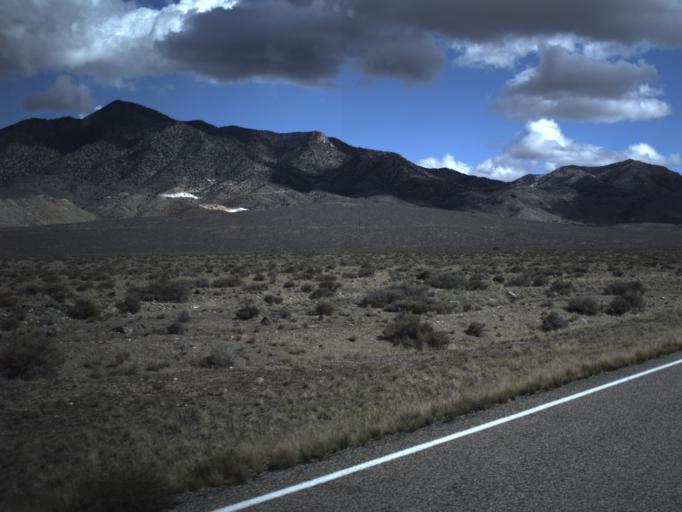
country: US
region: Utah
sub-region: Beaver County
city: Milford
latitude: 38.4493
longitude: -113.3419
